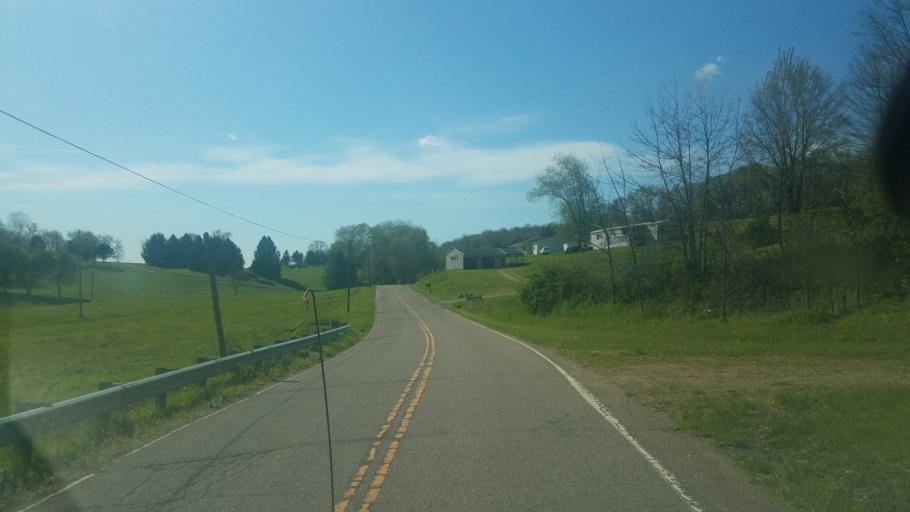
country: US
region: Ohio
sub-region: Coshocton County
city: Coshocton
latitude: 40.3325
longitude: -81.9011
